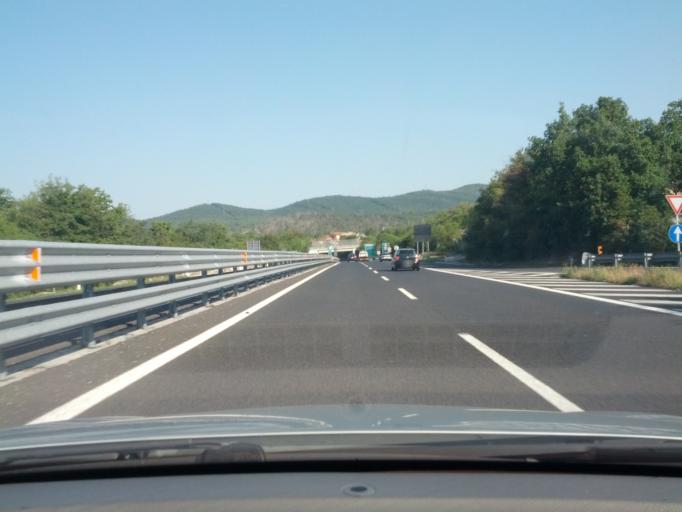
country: IT
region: Friuli Venezia Giulia
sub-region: Provincia di Trieste
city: Sistiana-Visogliano
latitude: 45.7705
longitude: 13.6446
